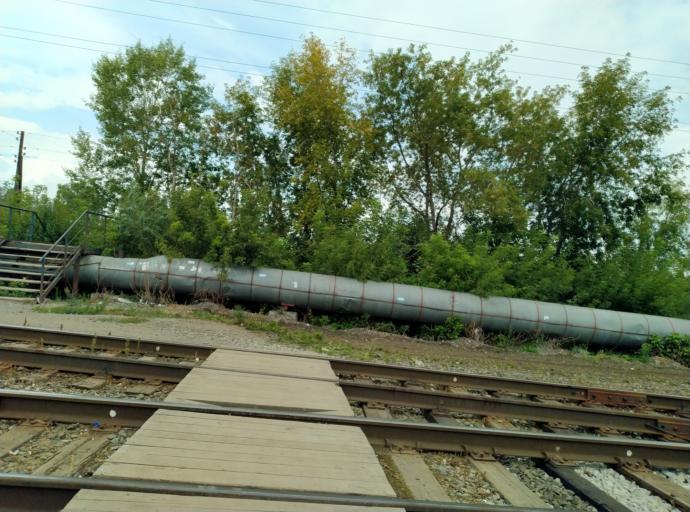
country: RU
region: Tomsk
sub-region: Tomskiy Rayon
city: Tomsk
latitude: 56.5254
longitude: 84.9556
